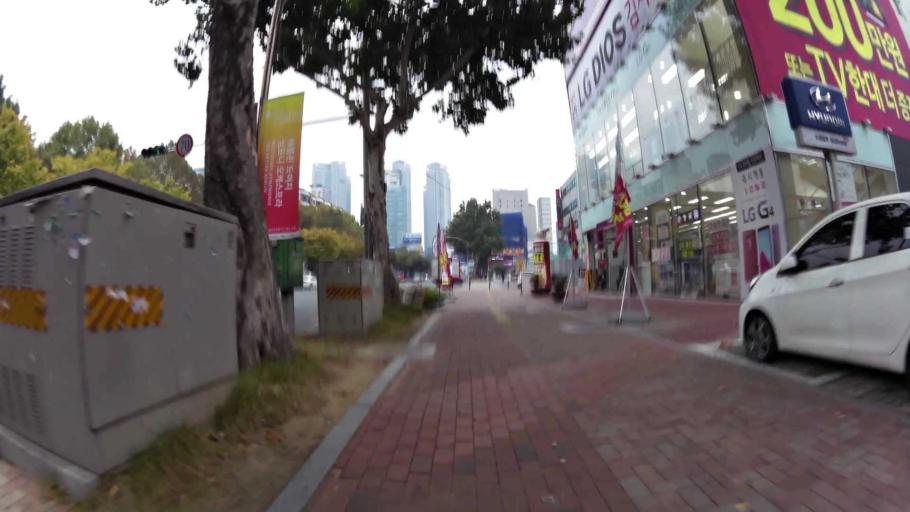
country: KR
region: Daegu
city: Daegu
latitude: 35.8593
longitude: 128.6201
